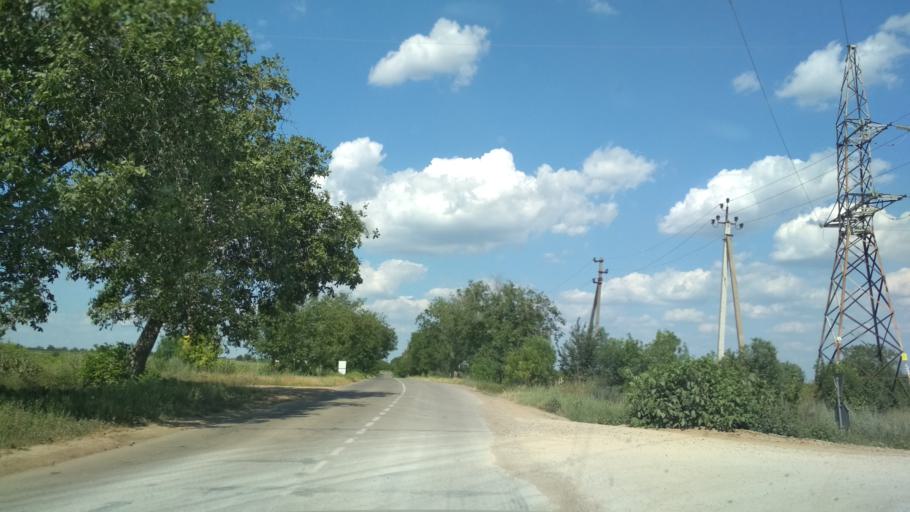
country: MD
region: Criuleni
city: Criuleni
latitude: 47.1687
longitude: 29.1828
